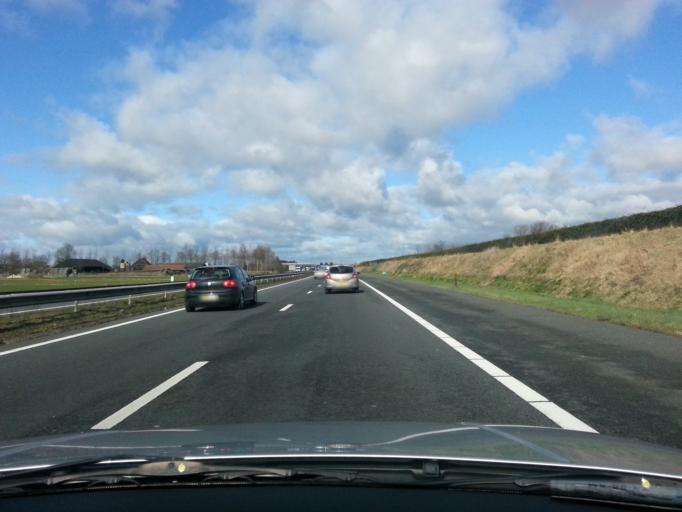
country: NL
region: Gelderland
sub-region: Gemeente Nijkerk
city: Nijkerk
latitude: 52.2181
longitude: 5.4505
